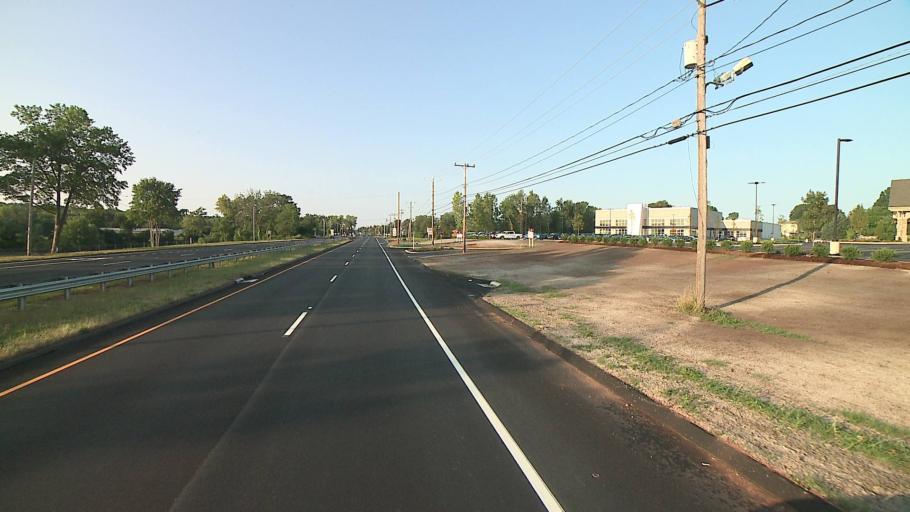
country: US
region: Connecticut
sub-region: Hartford County
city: Kensington
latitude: 41.6437
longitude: -72.7322
